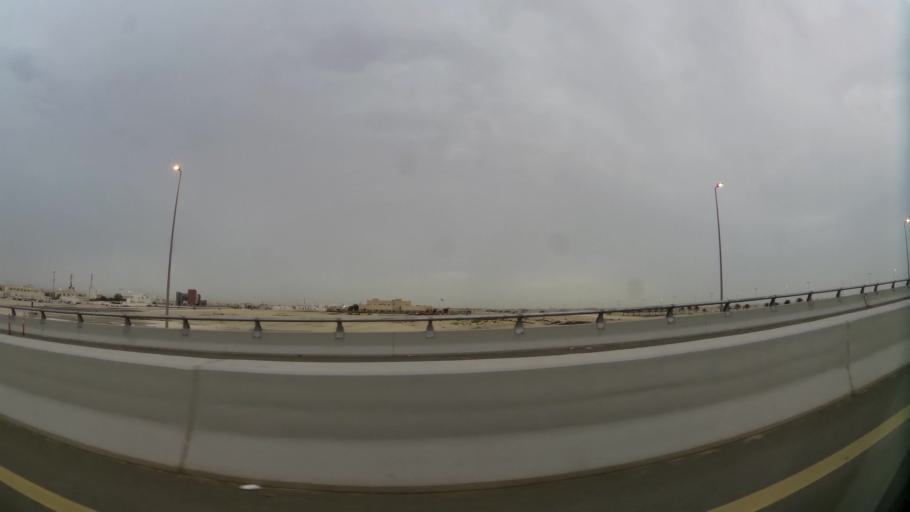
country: BH
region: Central Governorate
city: Dar Kulayb
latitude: 26.0817
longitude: 50.5134
